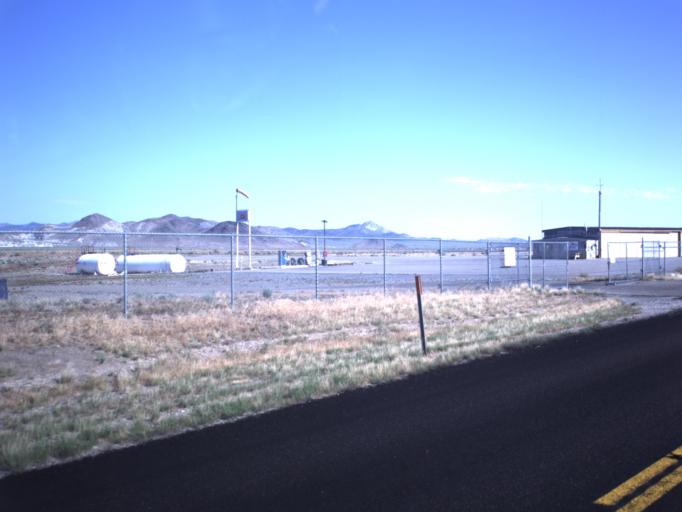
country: US
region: Utah
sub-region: Beaver County
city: Milford
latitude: 38.4181
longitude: -113.0099
